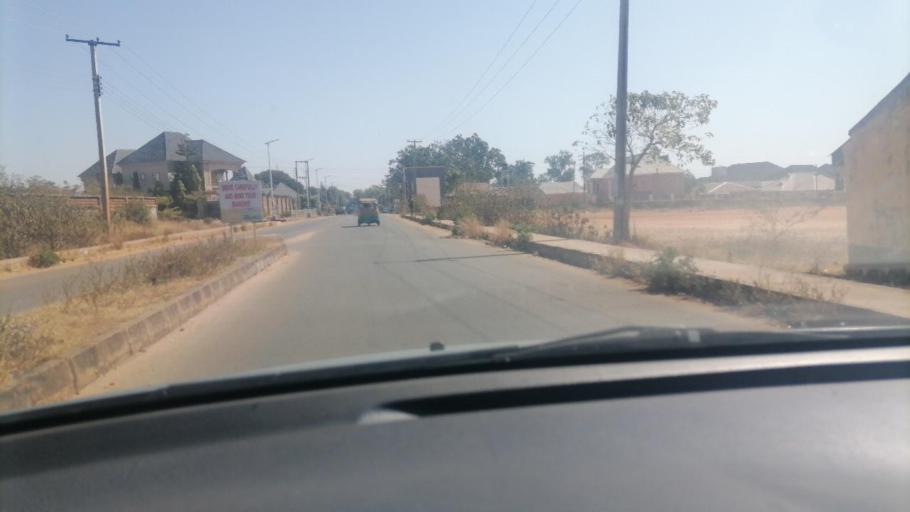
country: NG
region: Plateau
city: Jos
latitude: 9.8651
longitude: 8.9027
